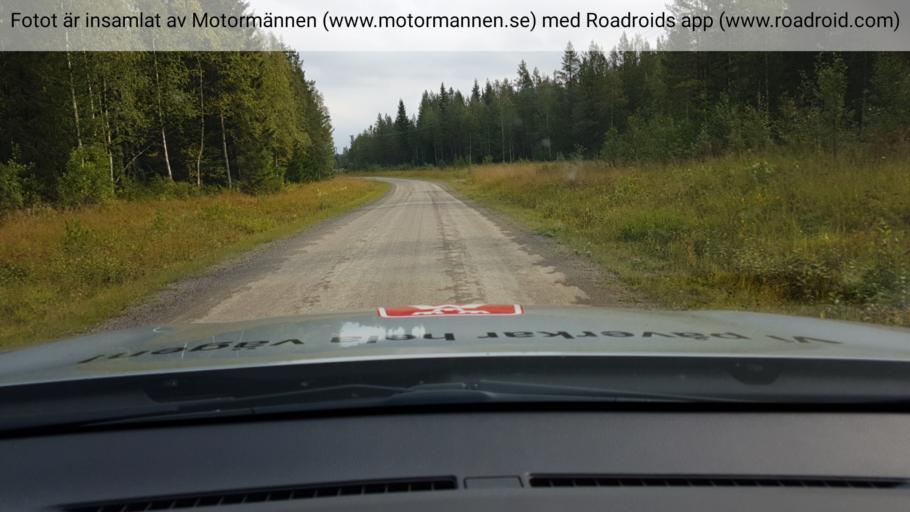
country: SE
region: Jaemtland
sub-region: Stroemsunds Kommun
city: Stroemsund
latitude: 63.7377
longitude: 15.4131
